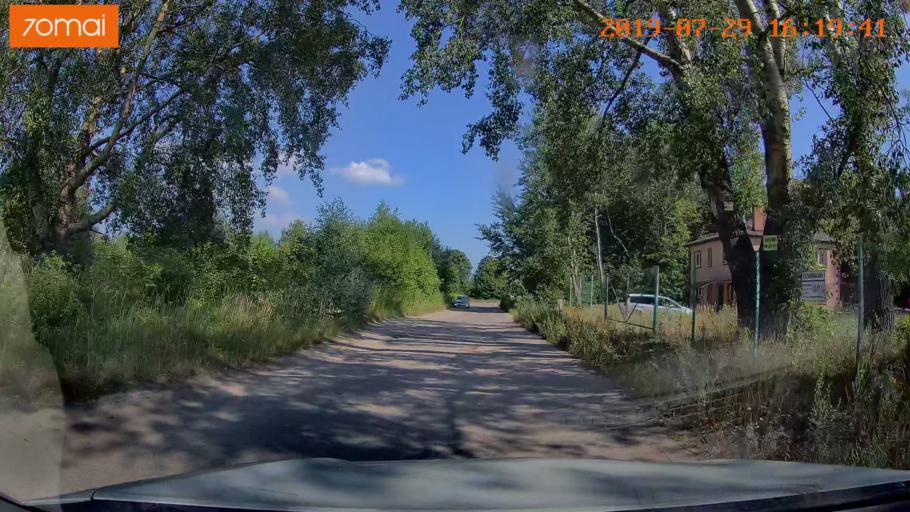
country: RU
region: Kaliningrad
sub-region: Gorod Kaliningrad
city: Baltiysk
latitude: 54.6790
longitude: 19.9259
